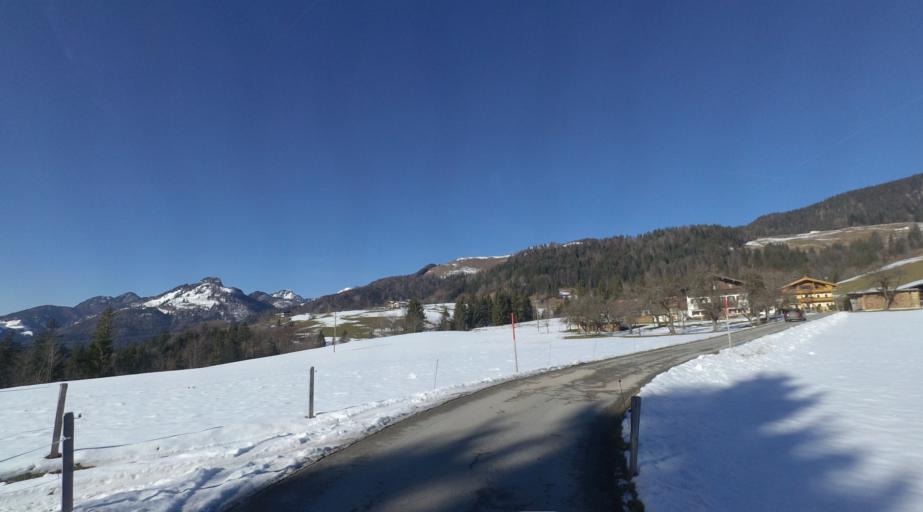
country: AT
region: Tyrol
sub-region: Politischer Bezirk Kitzbuhel
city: Kossen
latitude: 47.6775
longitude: 12.4301
